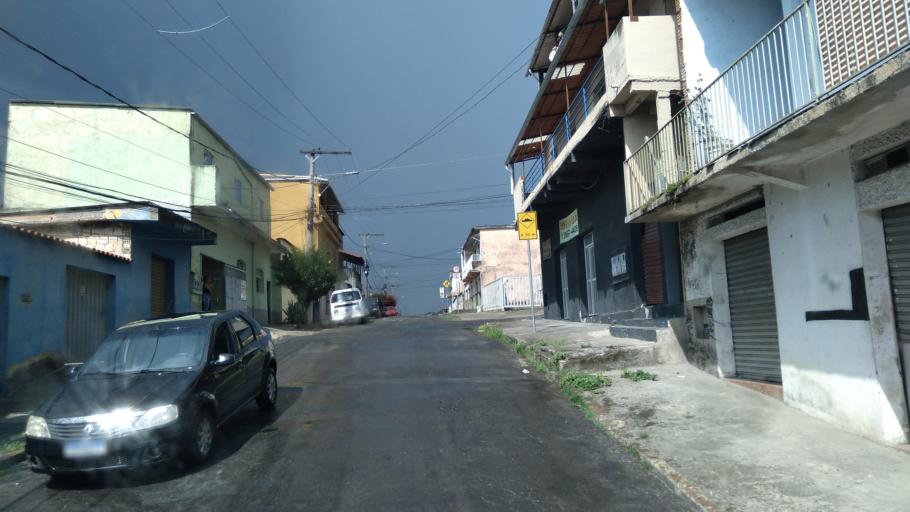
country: BR
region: Minas Gerais
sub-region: Contagem
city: Contagem
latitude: -19.9211
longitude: -44.0128
